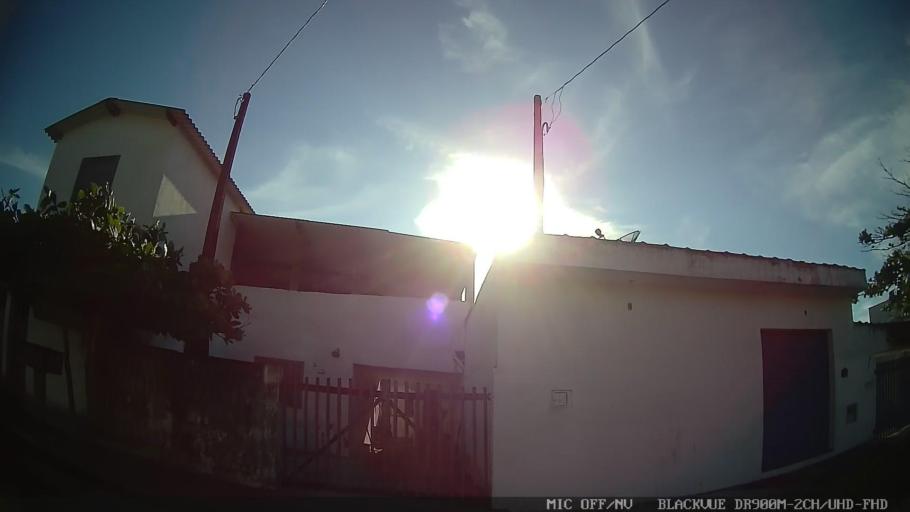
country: BR
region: Sao Paulo
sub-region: Iguape
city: Iguape
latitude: -24.7600
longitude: -47.5730
